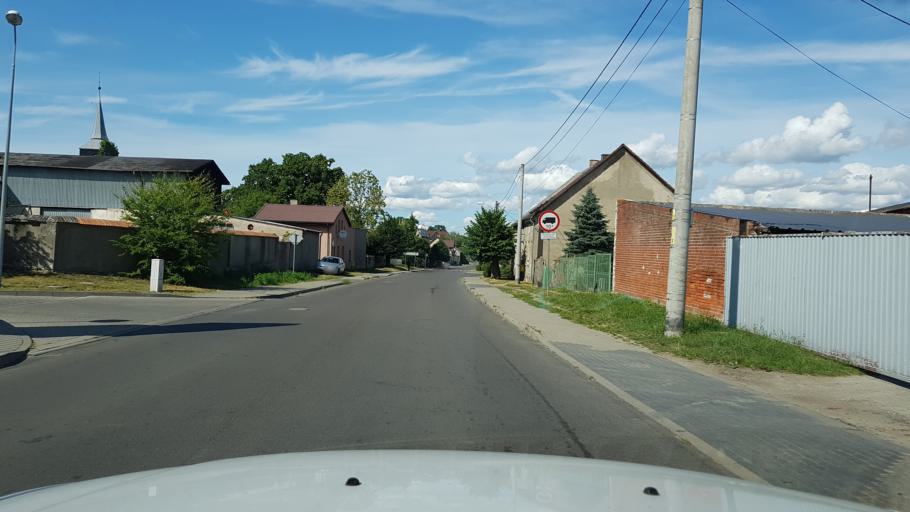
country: PL
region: West Pomeranian Voivodeship
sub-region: Powiat gryfinski
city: Stare Czarnowo
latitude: 53.2787
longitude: 14.7791
